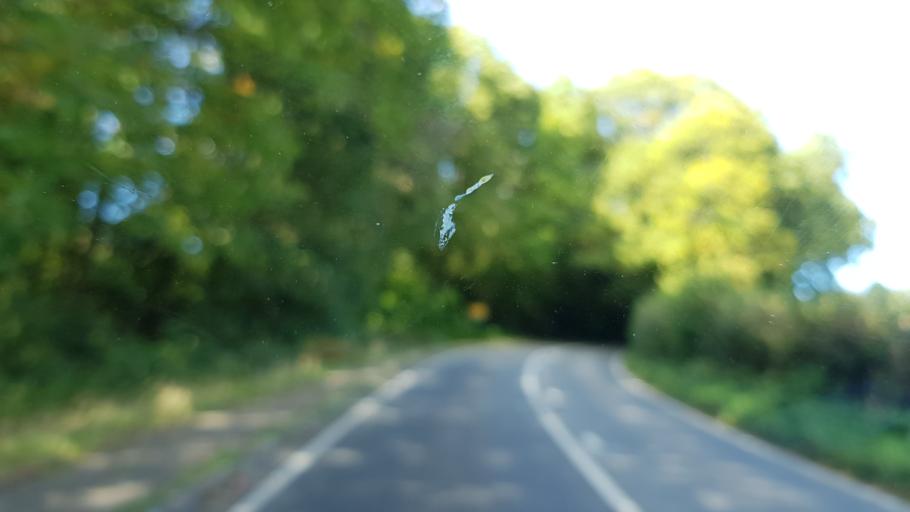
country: GB
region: England
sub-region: Surrey
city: Chiddingfold
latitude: 51.0601
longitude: -0.6438
